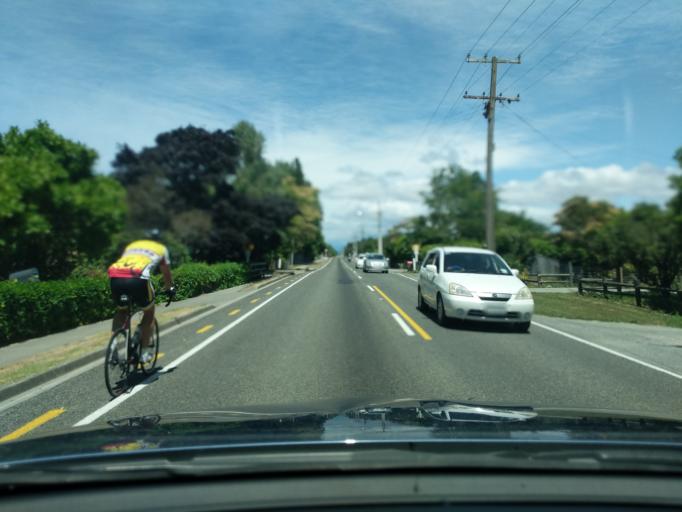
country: NZ
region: Tasman
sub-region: Tasman District
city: Motueka
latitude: -41.0781
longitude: 172.9974
